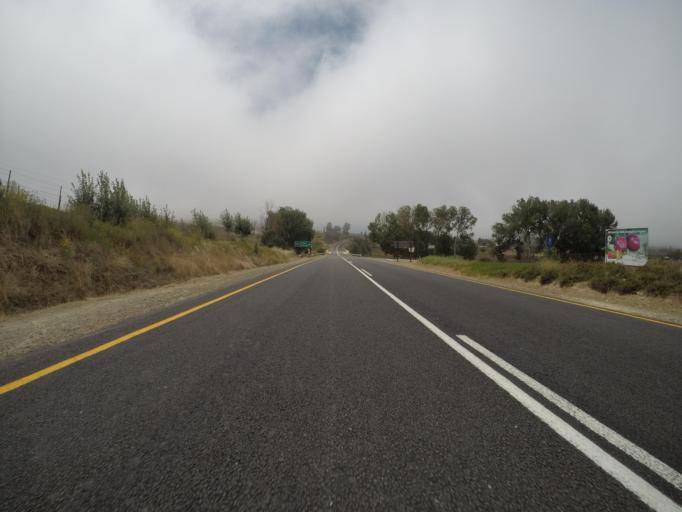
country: ZA
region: Western Cape
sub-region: Eden District Municipality
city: Knysna
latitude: -33.7257
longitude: 23.1641
